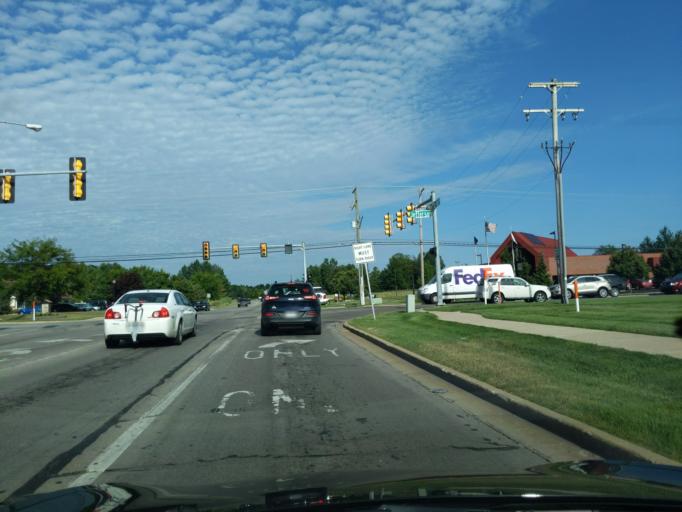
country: US
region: Michigan
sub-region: Midland County
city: Midland
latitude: 43.6593
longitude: -84.2278
